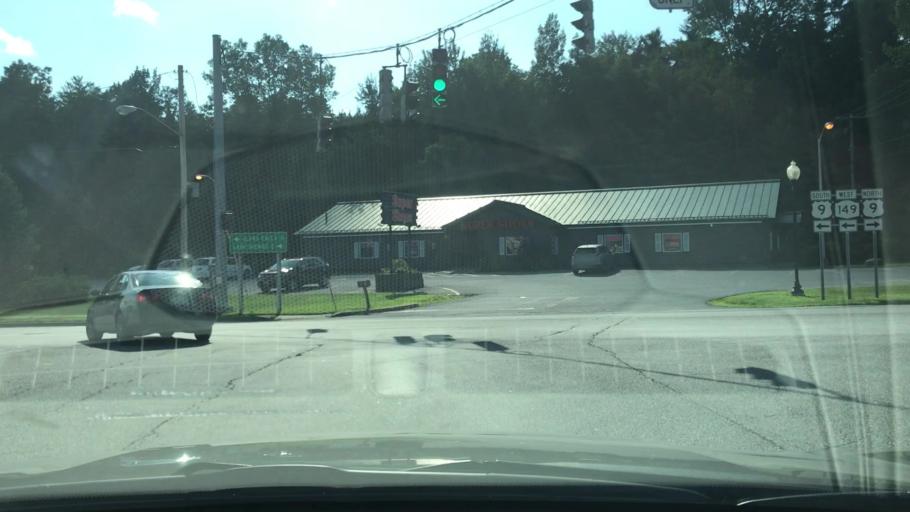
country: US
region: New York
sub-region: Warren County
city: Glens Falls North
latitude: 43.3693
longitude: -73.6978
